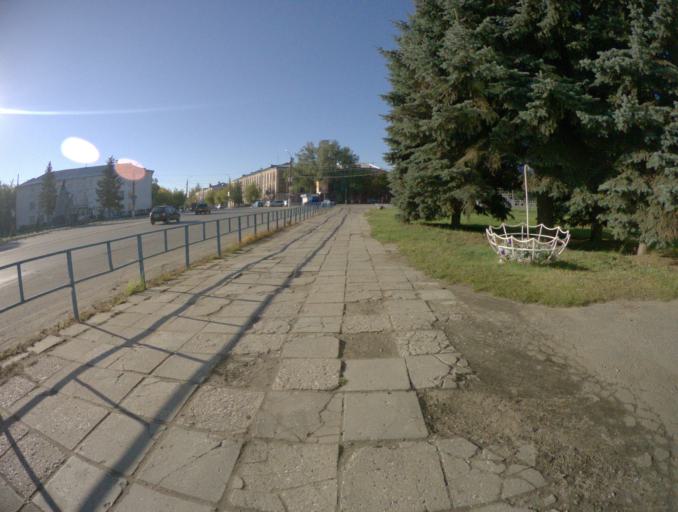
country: RU
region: Vladimir
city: Sobinka
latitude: 55.9941
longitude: 40.0182
